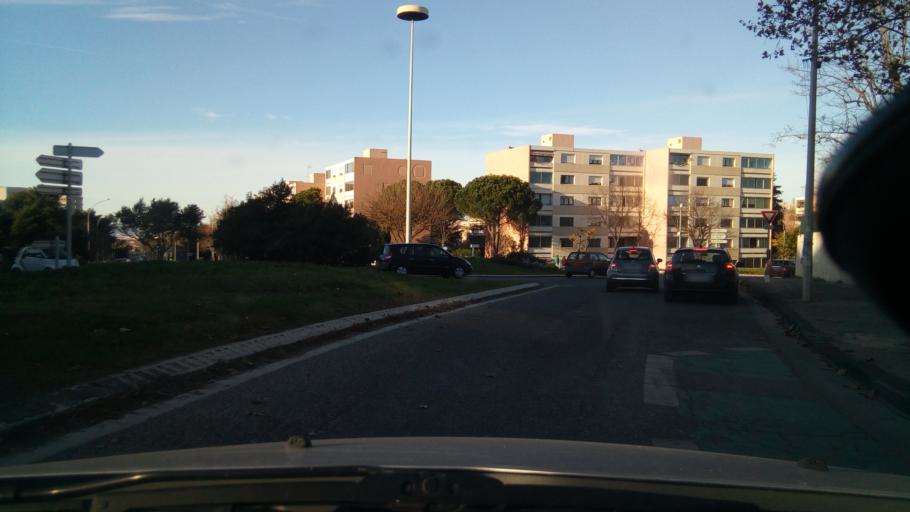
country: FR
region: Provence-Alpes-Cote d'Azur
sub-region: Departement des Bouches-du-Rhone
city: Marseille 09
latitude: 43.2456
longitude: 5.3953
